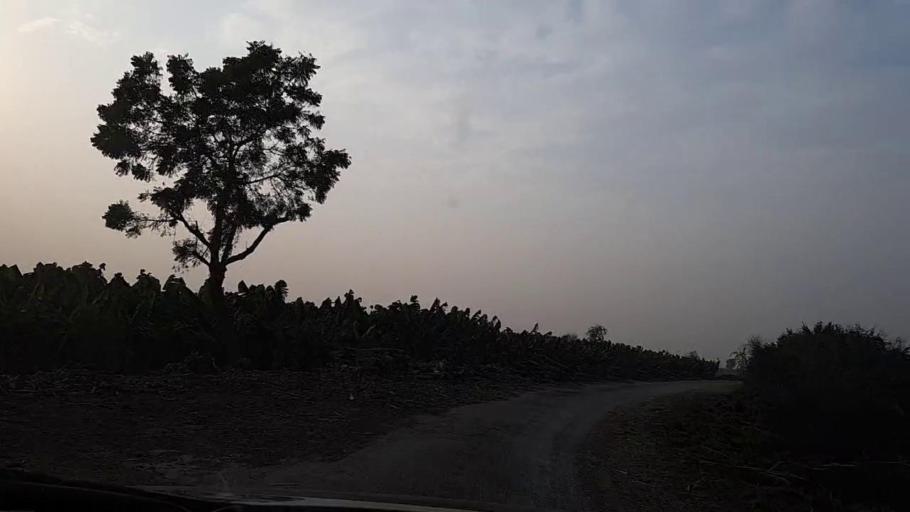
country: PK
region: Sindh
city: Nawabshah
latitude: 26.2944
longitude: 68.2786
